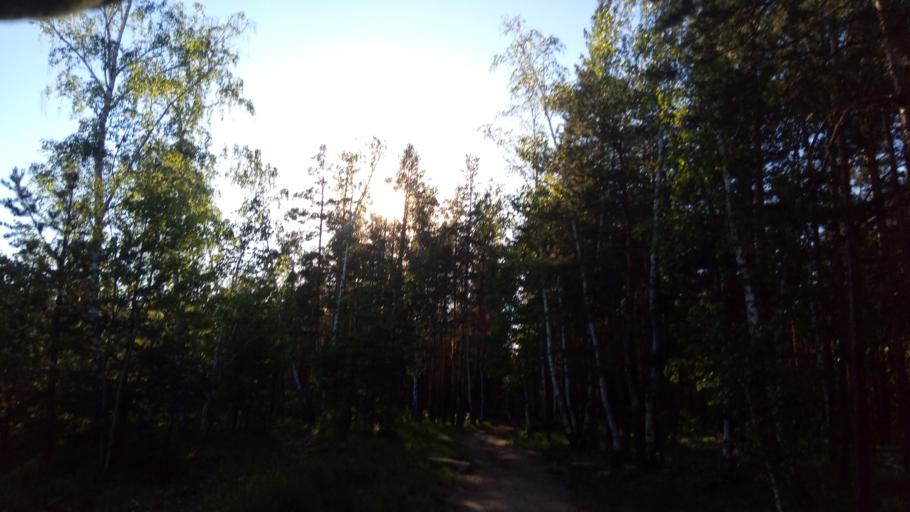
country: RU
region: Chelyabinsk
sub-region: Gorod Chelyabinsk
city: Chelyabinsk
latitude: 55.1269
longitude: 61.3418
